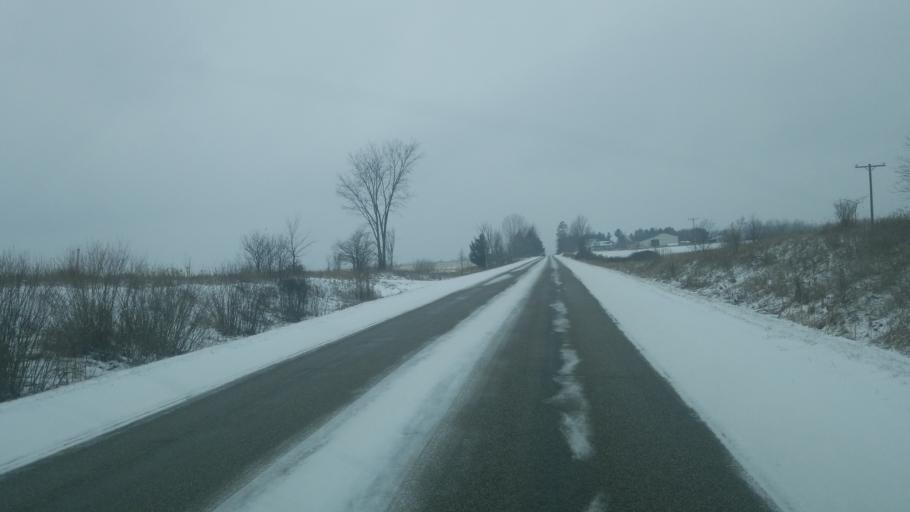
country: US
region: Michigan
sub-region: Osceola County
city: Evart
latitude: 44.1025
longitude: -85.1697
